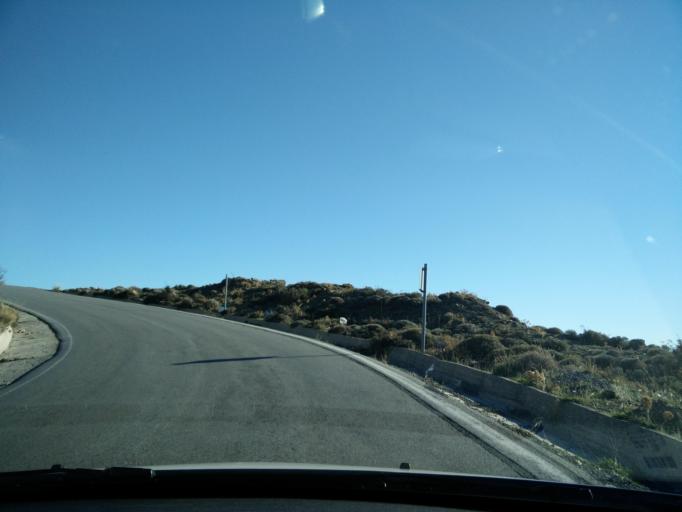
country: GR
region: Crete
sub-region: Nomos Irakleiou
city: Kastelli
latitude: 35.0447
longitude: 25.4231
